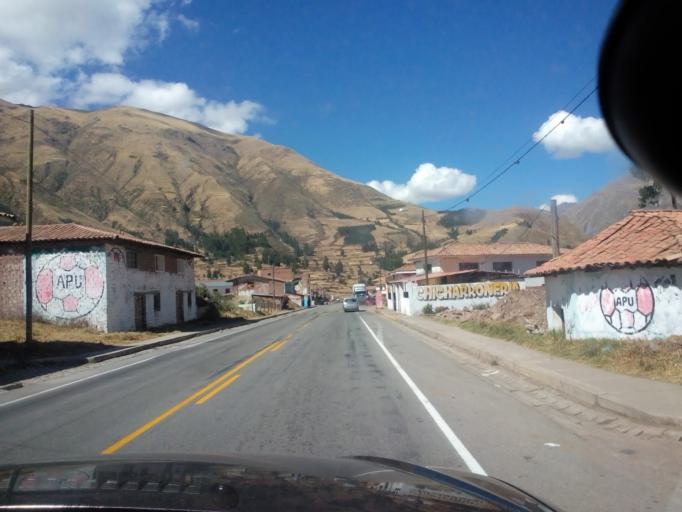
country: PE
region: Cusco
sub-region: Provincia de Quispicanchis
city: Cusipata
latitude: -13.9025
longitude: -71.5001
